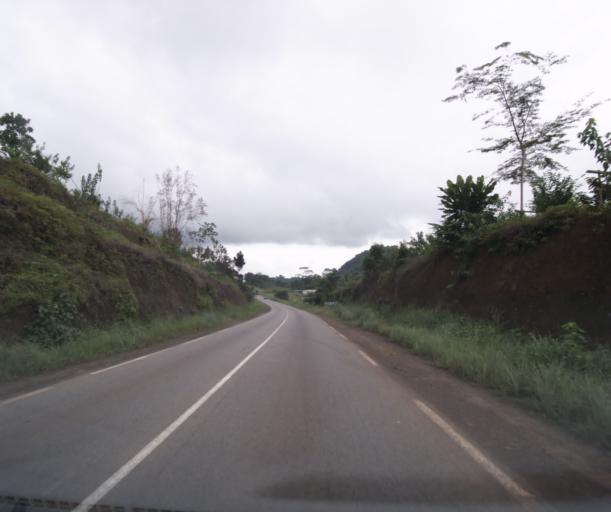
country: CM
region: Littoral
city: Edea
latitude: 3.8037
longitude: 10.2279
